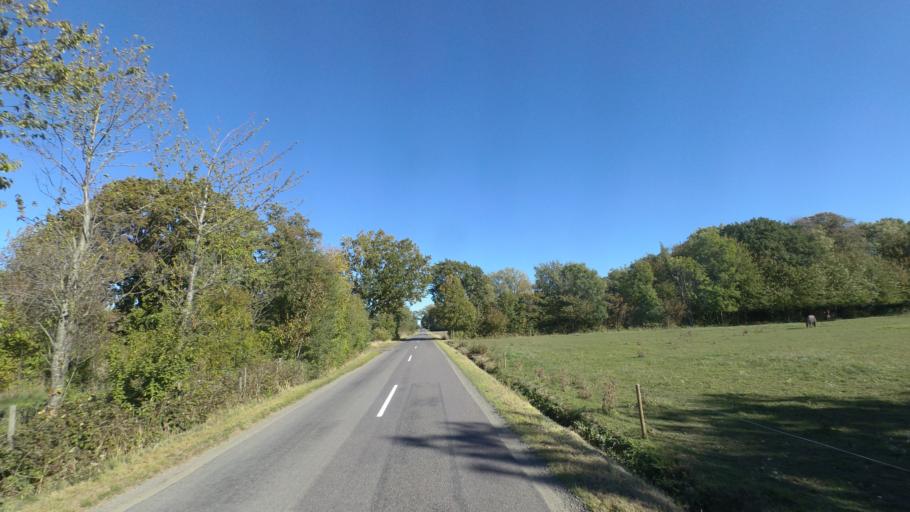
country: DK
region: Capital Region
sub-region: Bornholm Kommune
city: Nexo
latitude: 55.1099
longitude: 15.1134
